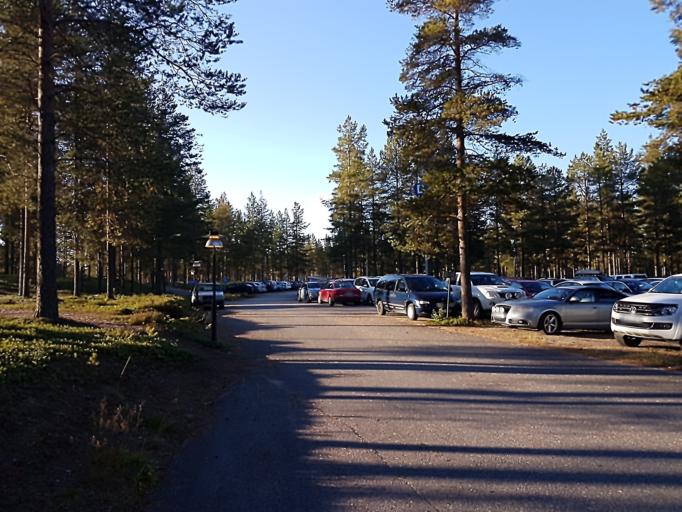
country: SE
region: Norrbotten
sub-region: Lulea Kommun
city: Bergnaset
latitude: 65.5491
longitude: 22.1267
